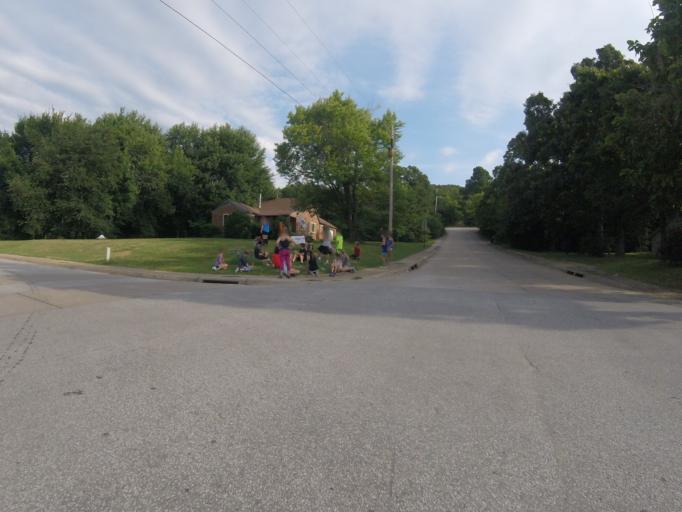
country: US
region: Arkansas
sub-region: Washington County
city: Fayetteville
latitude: 36.0597
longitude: -94.1893
